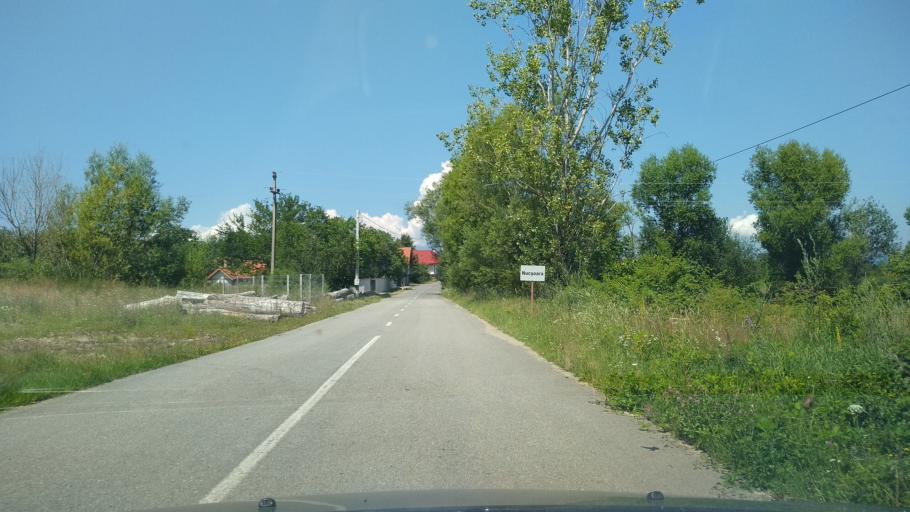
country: RO
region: Hunedoara
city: Salasu de Sus
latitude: 45.4837
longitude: 22.9300
